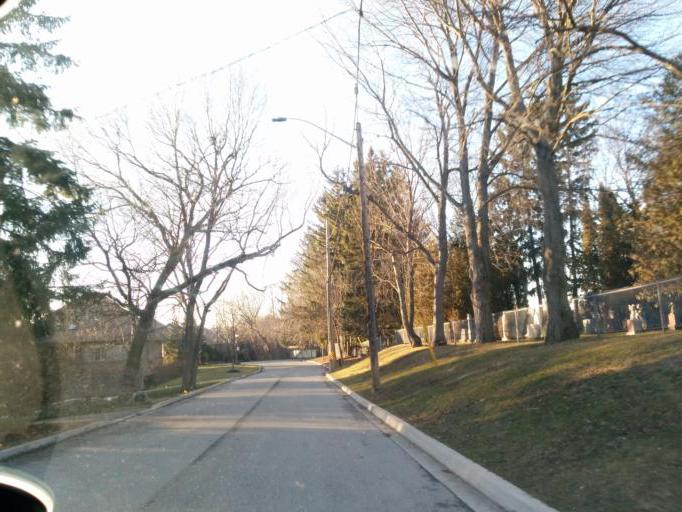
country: CA
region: Ontario
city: Mississauga
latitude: 43.5615
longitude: -79.6125
